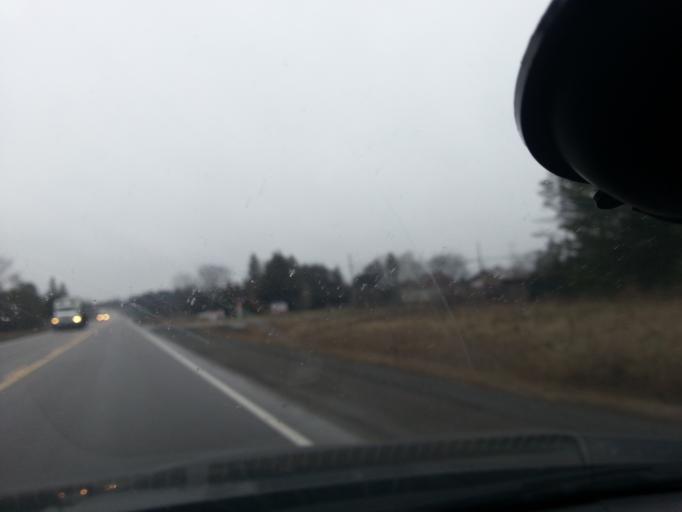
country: CA
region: Ontario
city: Quinte West
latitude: 44.4944
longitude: -77.6377
